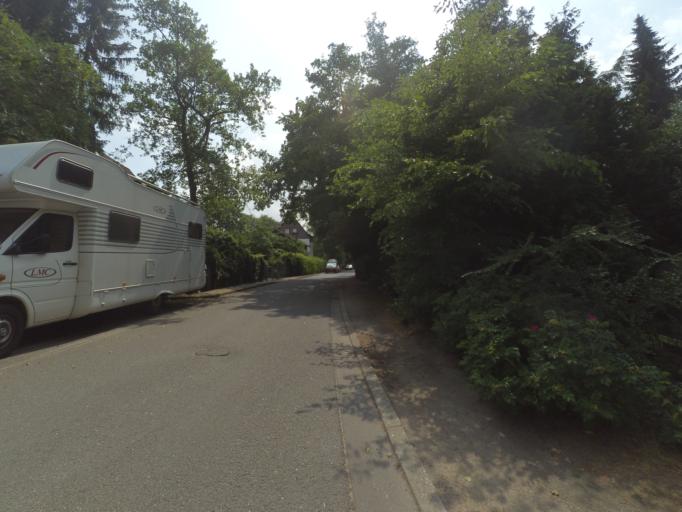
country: DE
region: Hamburg
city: Eidelstedt
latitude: 53.6315
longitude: 9.9362
